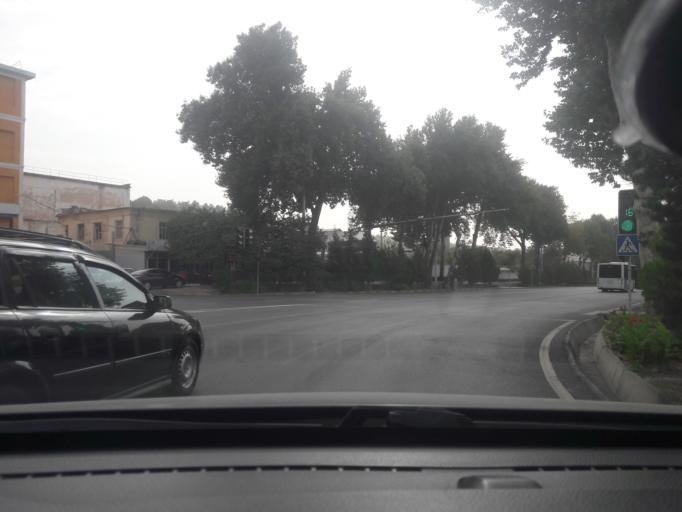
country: TJ
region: Dushanbe
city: Dushanbe
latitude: 38.5787
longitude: 68.8011
